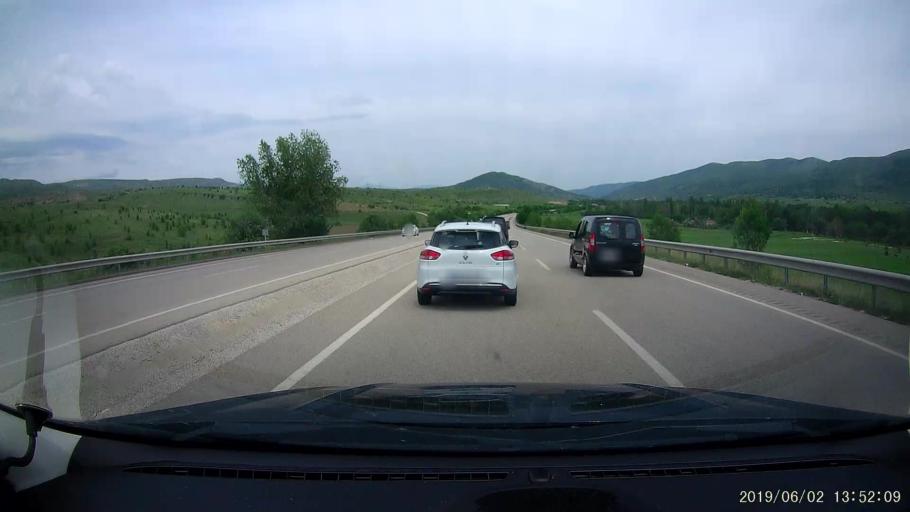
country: TR
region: Cankiri
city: Beloren
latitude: 40.8461
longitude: 33.3937
